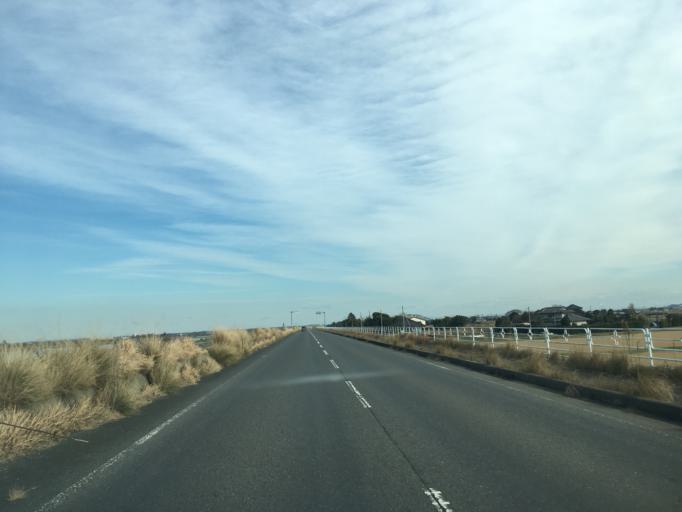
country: JP
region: Chiba
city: Katori-shi
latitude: 35.9085
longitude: 140.4347
